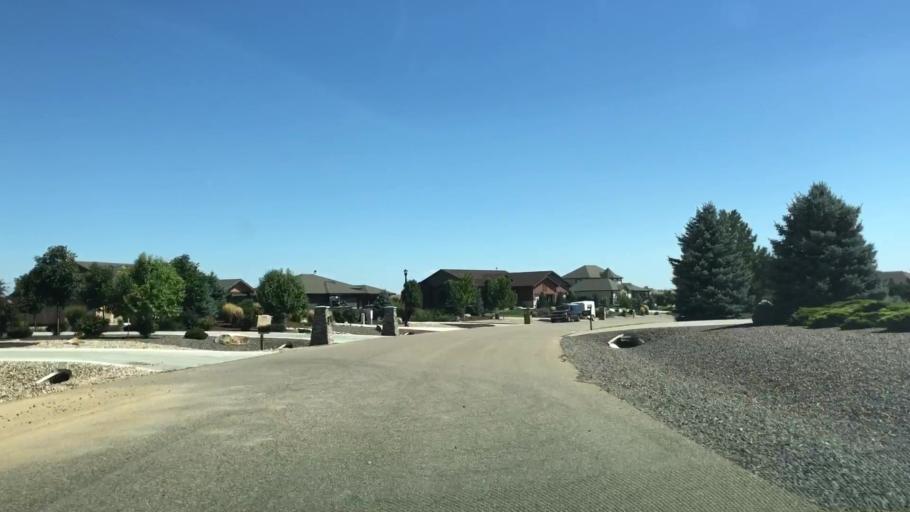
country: US
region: Colorado
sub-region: Weld County
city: Windsor
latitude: 40.4488
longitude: -104.9476
